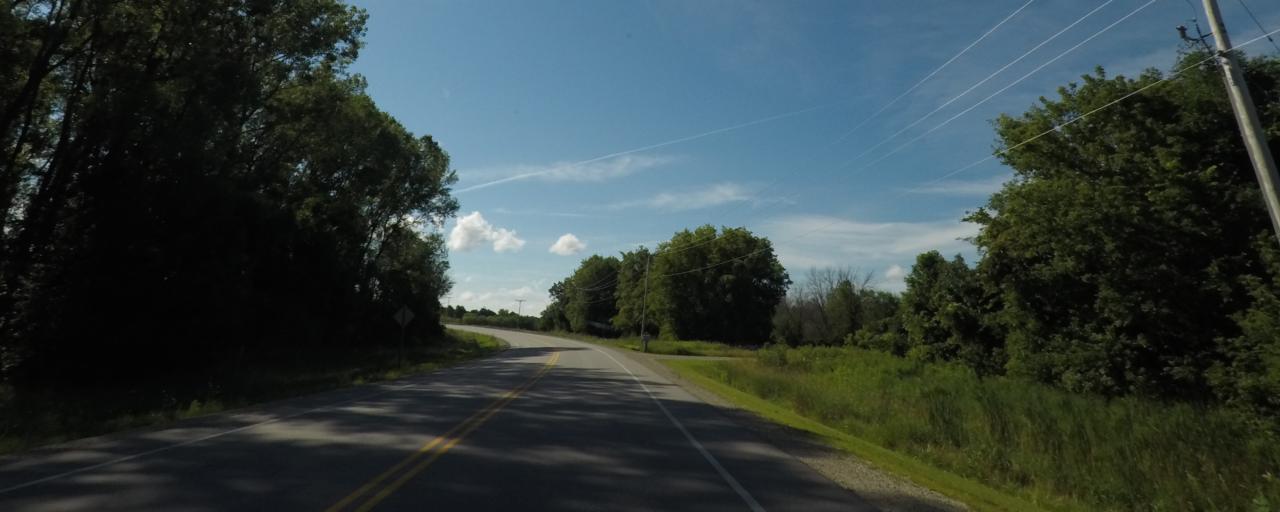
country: US
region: Wisconsin
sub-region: Jefferson County
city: Ixonia
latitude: 43.0710
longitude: -88.6355
